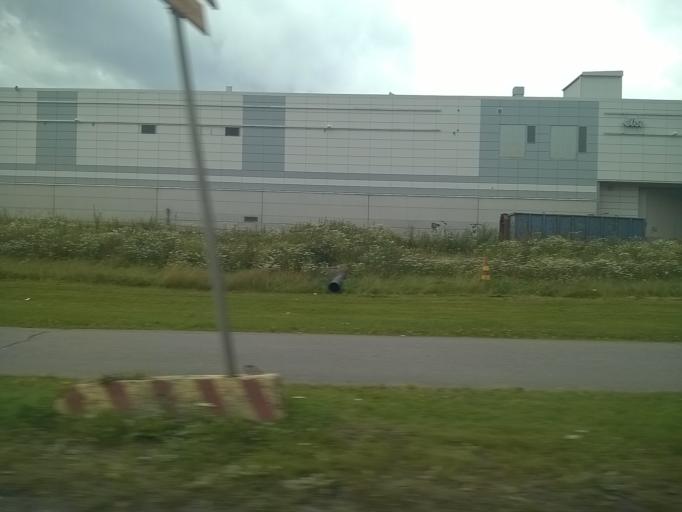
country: FI
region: Pirkanmaa
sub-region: Tampere
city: Tampere
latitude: 61.4909
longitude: 23.8226
